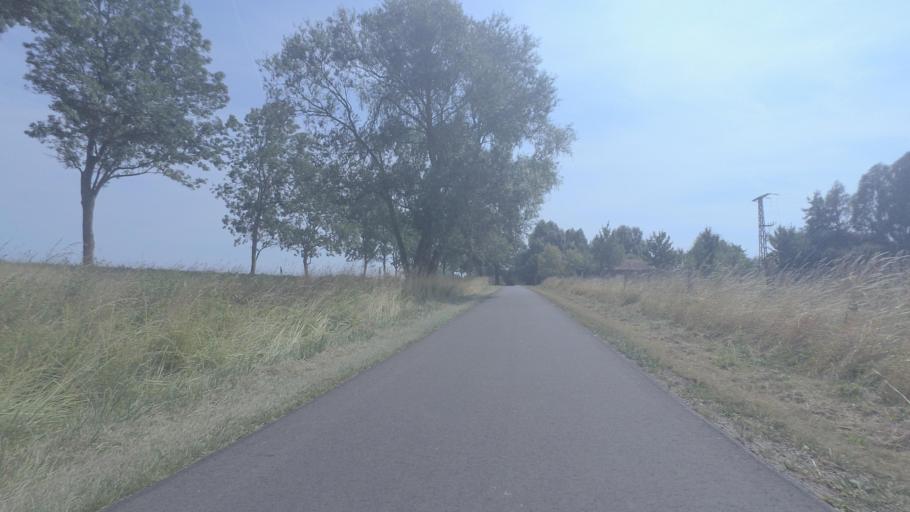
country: DE
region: Mecklenburg-Vorpommern
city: Garz
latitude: 54.2652
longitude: 13.3487
